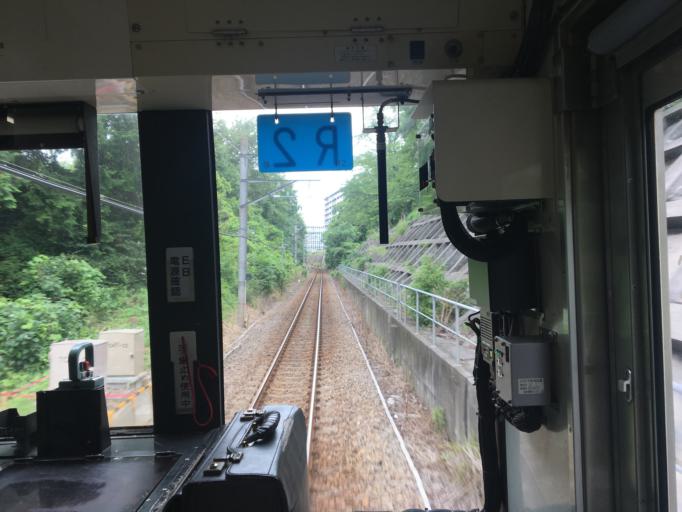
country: JP
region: Kanagawa
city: Zama
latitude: 35.5609
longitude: 139.3600
